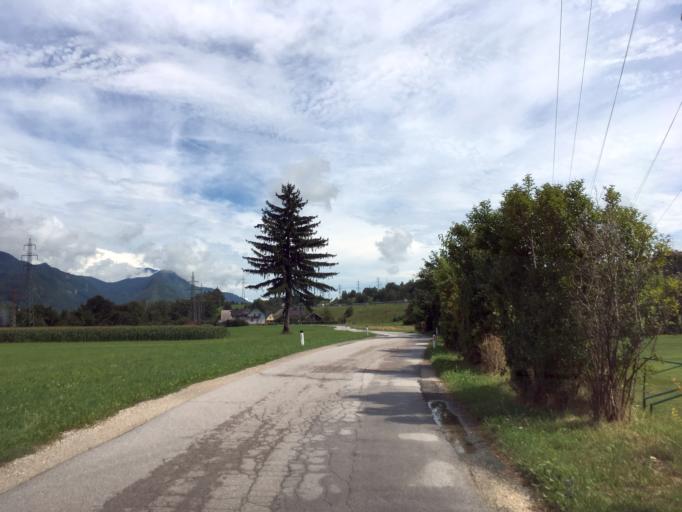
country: SI
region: Jesenice
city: Slovenski Javornik
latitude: 46.4168
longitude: 14.0957
